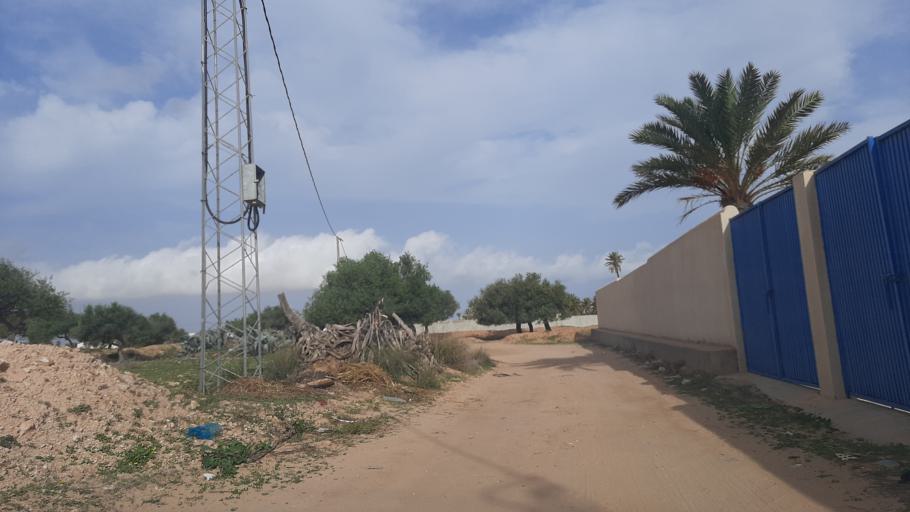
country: TN
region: Madanin
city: Midoun
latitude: 33.8041
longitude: 11.0256
